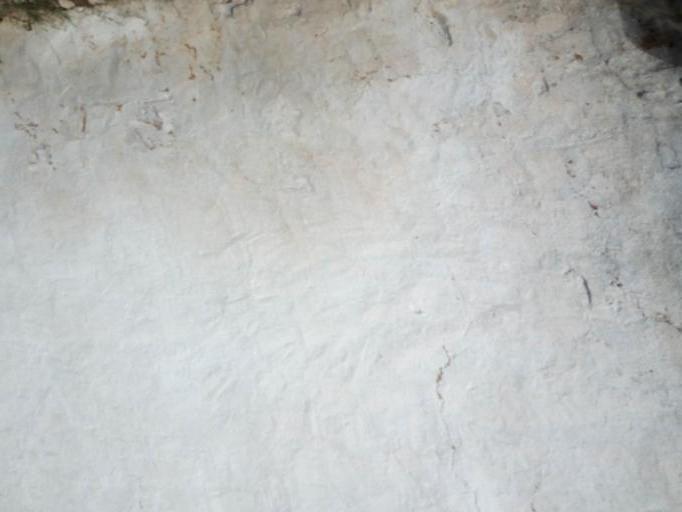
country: PT
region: Faro
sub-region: Faro
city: Santa Barbara de Nexe
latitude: 37.1185
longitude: -7.9582
